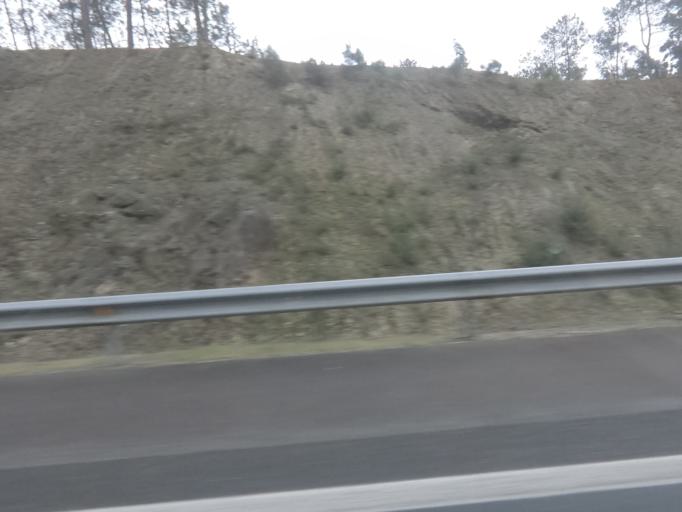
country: ES
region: Galicia
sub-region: Provincia da Coruna
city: Vedra
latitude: 42.8068
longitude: -8.4817
